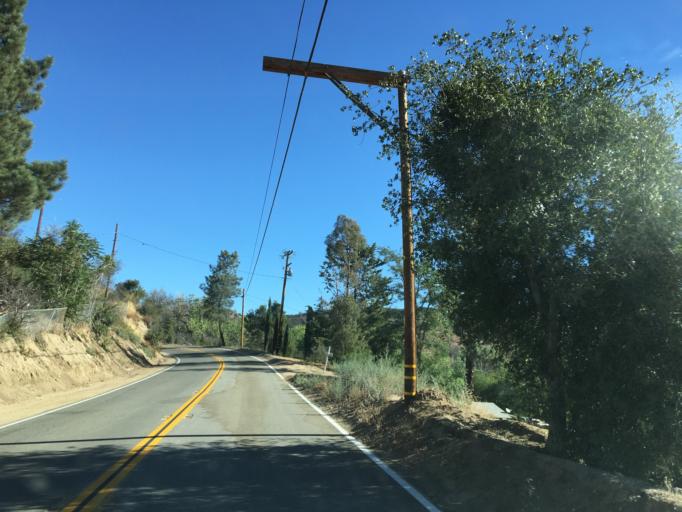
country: US
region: California
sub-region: Los Angeles County
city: Green Valley
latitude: 34.6692
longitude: -118.4545
